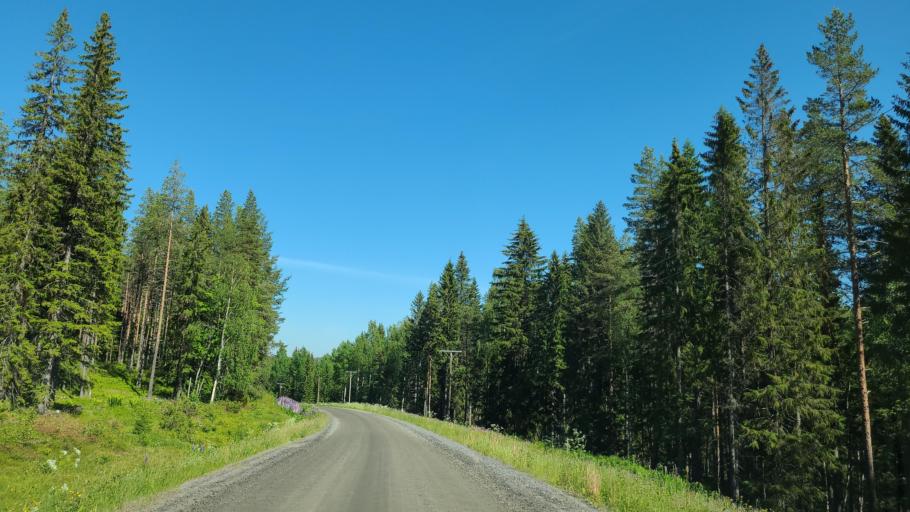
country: SE
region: Vaesterbotten
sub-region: Bjurholms Kommun
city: Bjurholm
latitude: 63.6398
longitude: 19.1511
